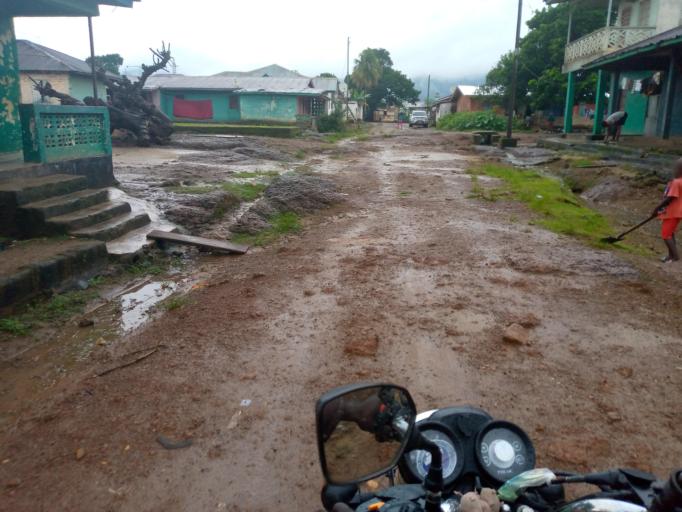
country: SL
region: Eastern Province
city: Kenema
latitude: 7.8840
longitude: -11.1833
